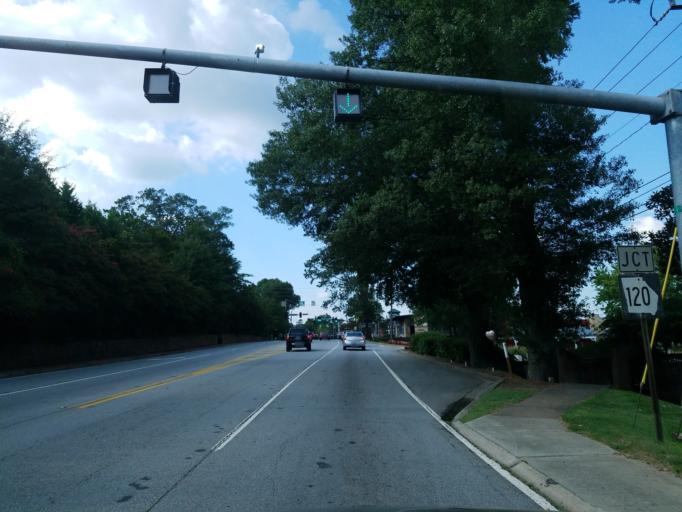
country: US
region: Georgia
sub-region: Fulton County
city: Roswell
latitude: 34.0129
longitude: -84.3628
